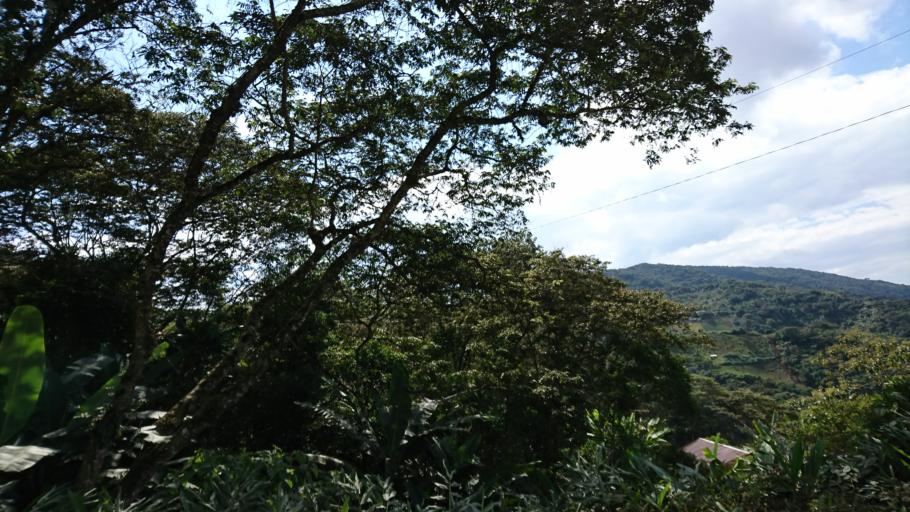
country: BO
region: La Paz
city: Coroico
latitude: -16.1182
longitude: -67.7656
